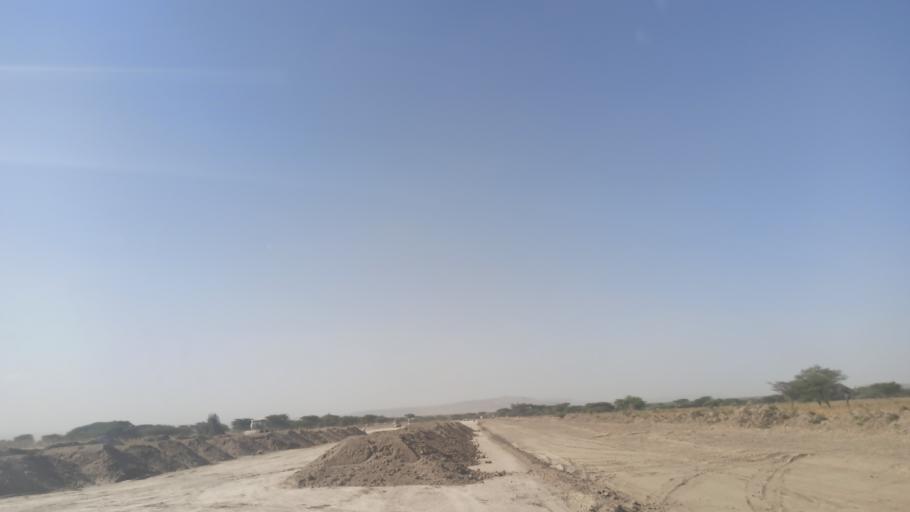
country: ET
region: Oromiya
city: Ziway
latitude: 7.7447
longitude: 38.6179
